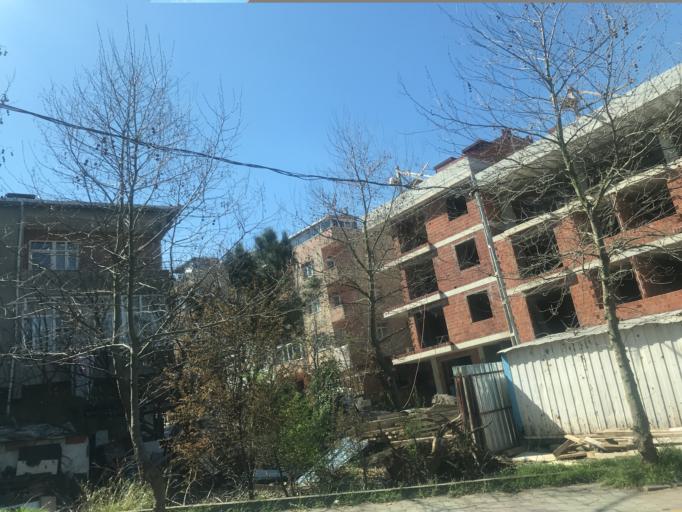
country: TR
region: Istanbul
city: Samandira
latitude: 41.0340
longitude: 29.1798
